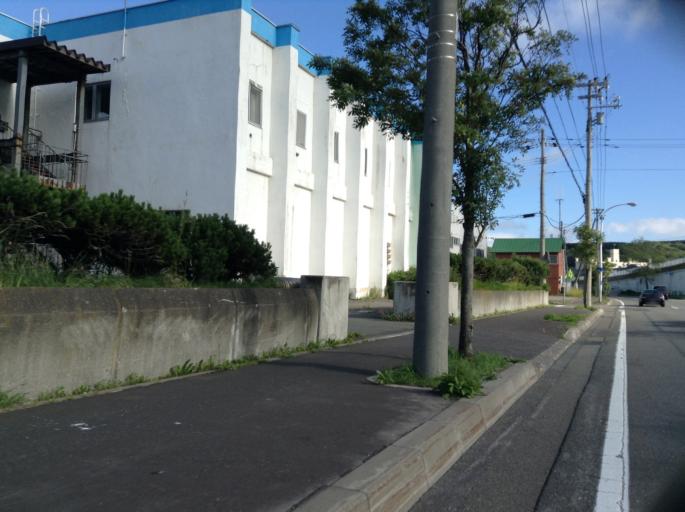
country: JP
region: Hokkaido
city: Wakkanai
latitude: 45.4063
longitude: 141.6758
